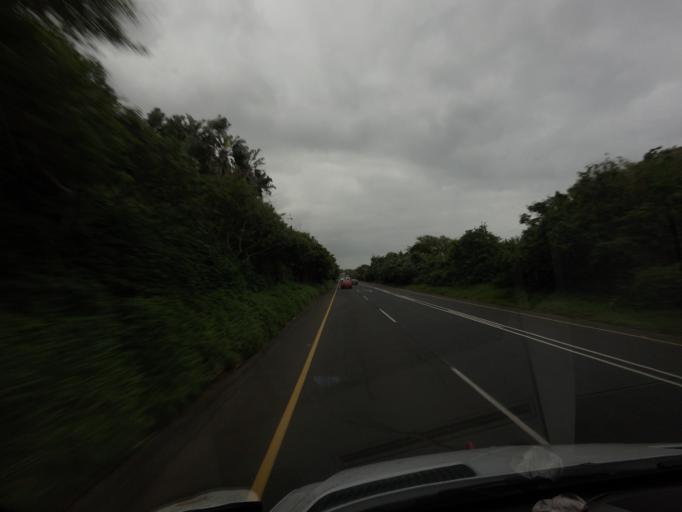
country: ZA
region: KwaZulu-Natal
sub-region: iLembe District Municipality
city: Ballitoville
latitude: -29.5859
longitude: 31.1738
